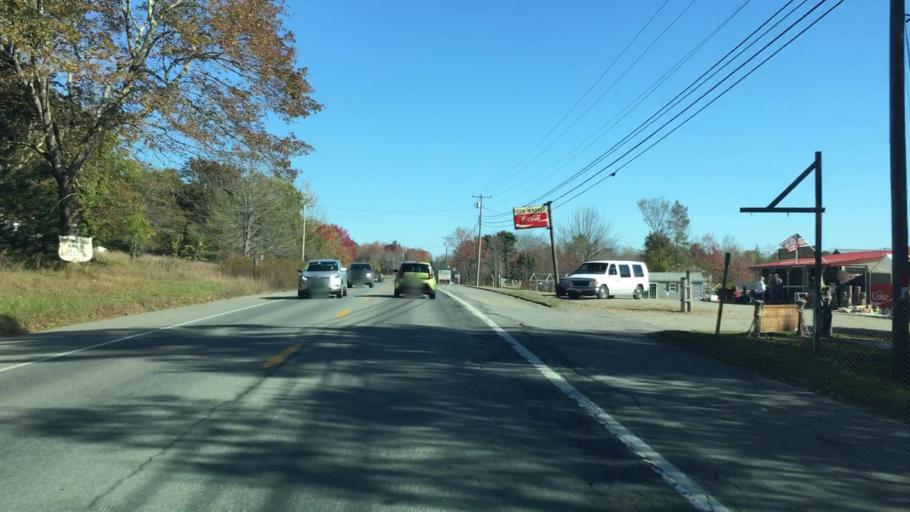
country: US
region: Maine
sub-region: Waldo County
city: Stockton Springs
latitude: 44.4777
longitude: -68.8776
